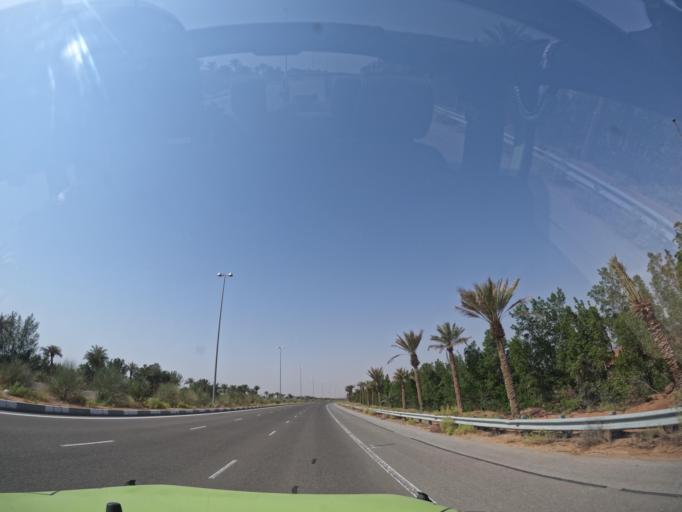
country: AE
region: Abu Dhabi
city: Al Ain
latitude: 24.2185
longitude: 55.6159
